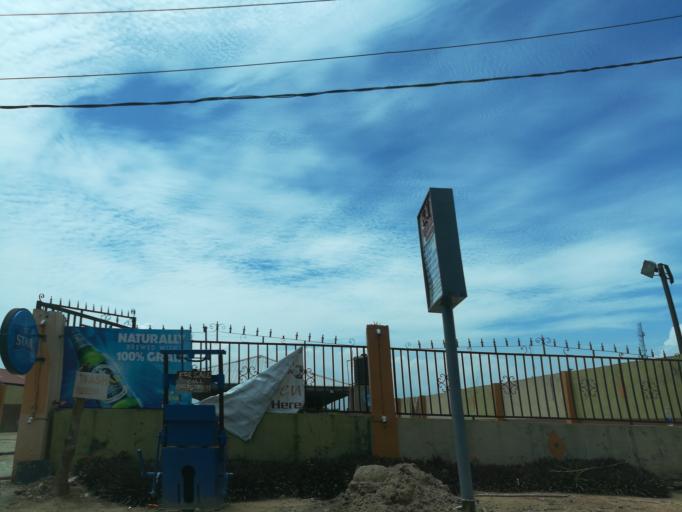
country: NG
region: Lagos
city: Ebute Ikorodu
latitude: 6.5857
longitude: 3.4924
